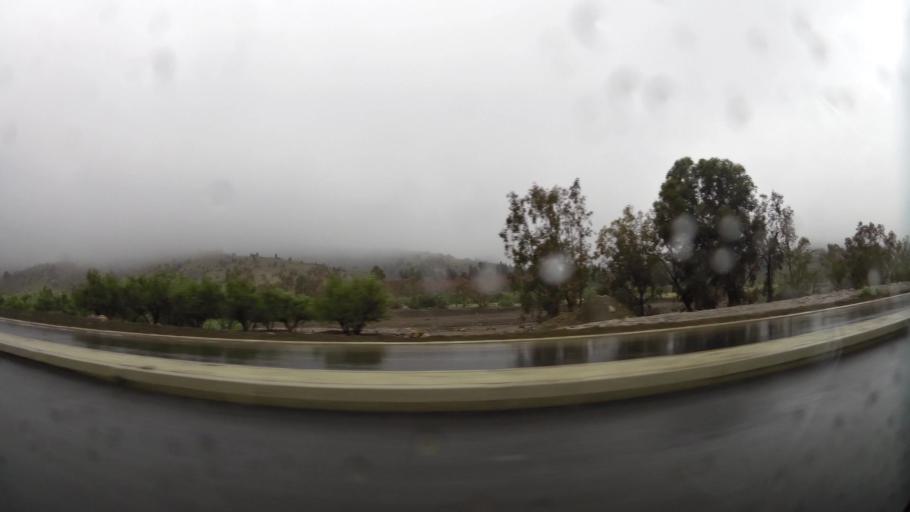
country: MA
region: Taza-Al Hoceima-Taounate
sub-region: Taza
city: Aknoul
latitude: 34.7976
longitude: -3.7438
